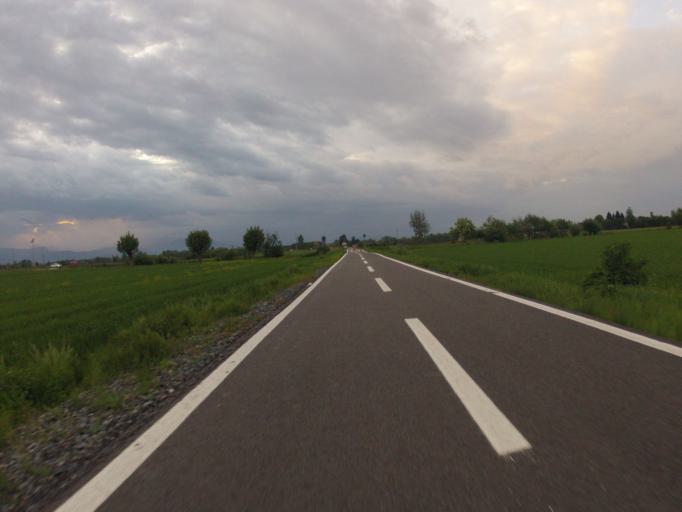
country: IT
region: Piedmont
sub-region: Provincia di Torino
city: Villafranca Piemonte
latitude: 44.8014
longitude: 7.5041
